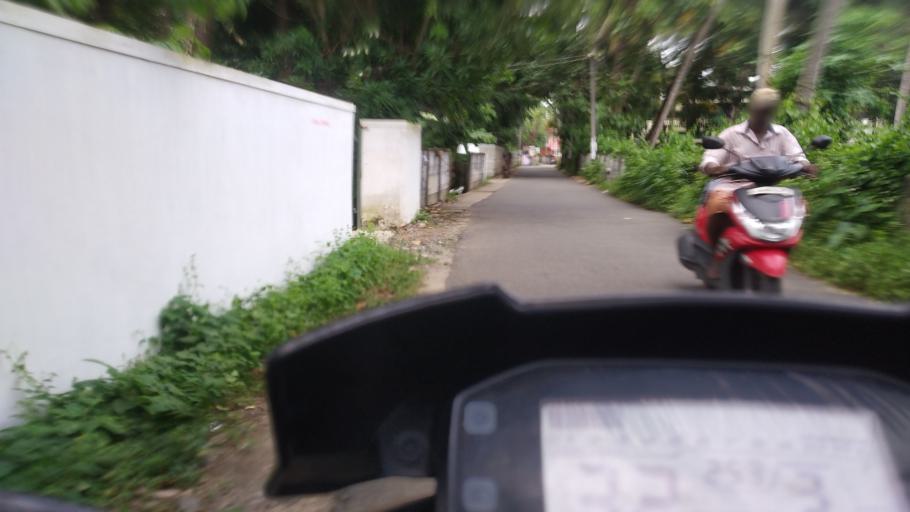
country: IN
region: Kerala
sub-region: Ernakulam
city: Elur
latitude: 10.0908
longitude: 76.2068
